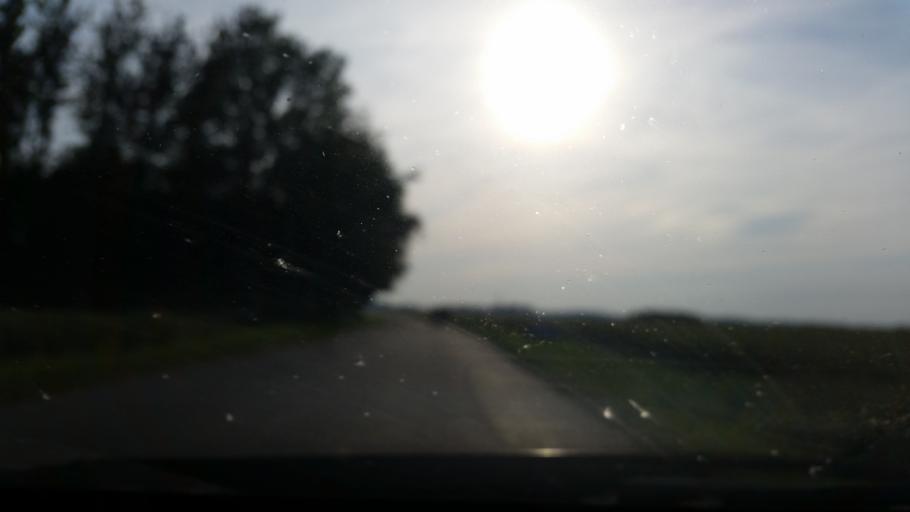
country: DK
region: Central Jutland
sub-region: Odder Kommune
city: Odder
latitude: 55.8919
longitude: 10.1400
